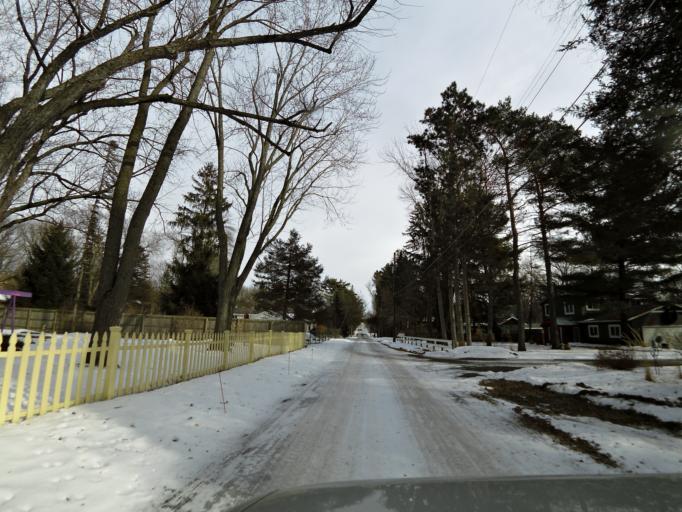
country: US
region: Minnesota
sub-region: Washington County
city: Lake Saint Croix Beach
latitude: 44.9133
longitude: -92.7754
